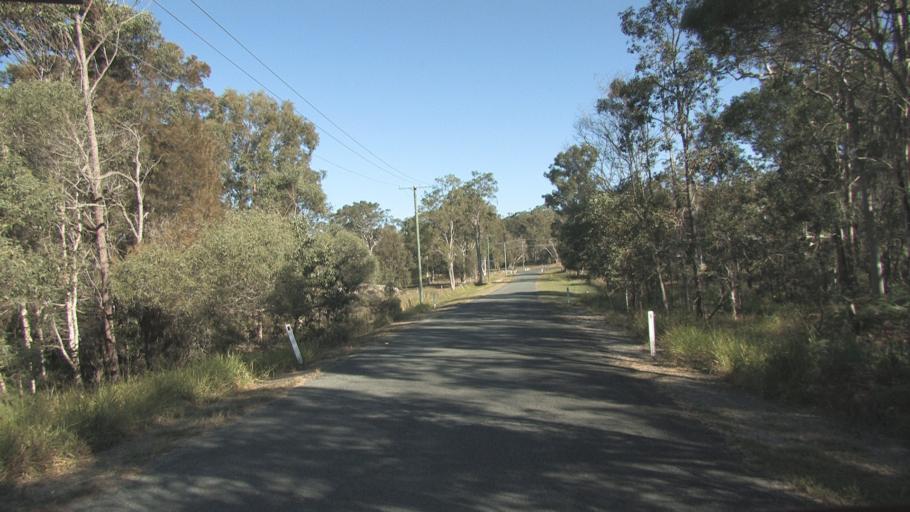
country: AU
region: Queensland
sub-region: Logan
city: Logan Reserve
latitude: -27.7315
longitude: 153.0827
